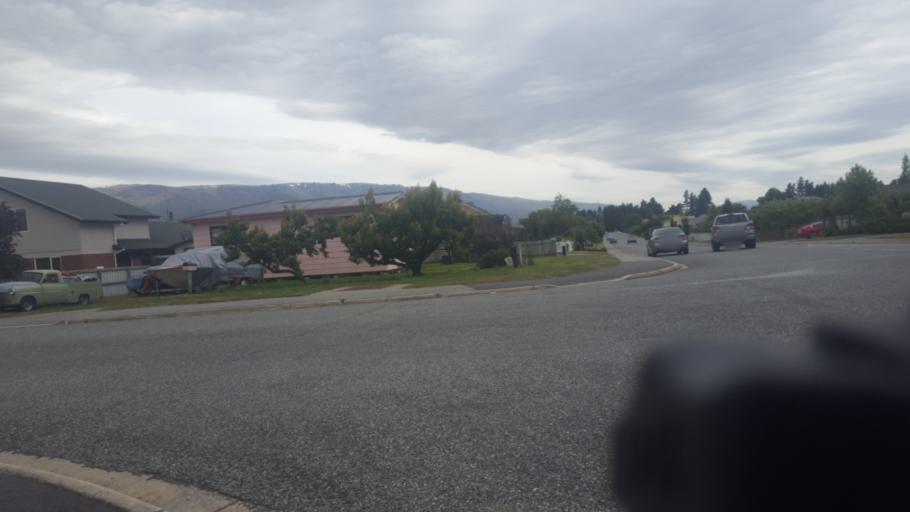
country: NZ
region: Otago
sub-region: Queenstown-Lakes District
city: Wanaka
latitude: -45.0448
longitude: 169.2004
